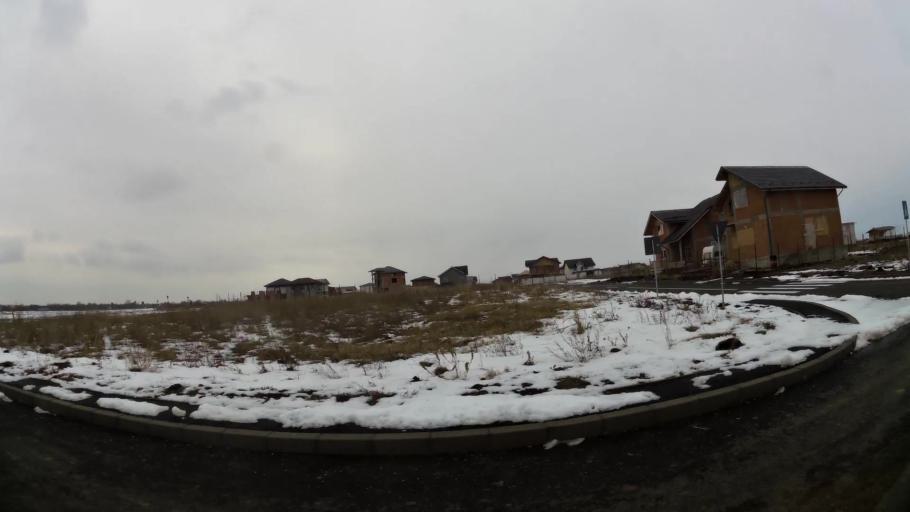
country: RO
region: Ilfov
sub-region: Comuna Tunari
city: Tunari
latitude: 44.5500
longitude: 26.1595
